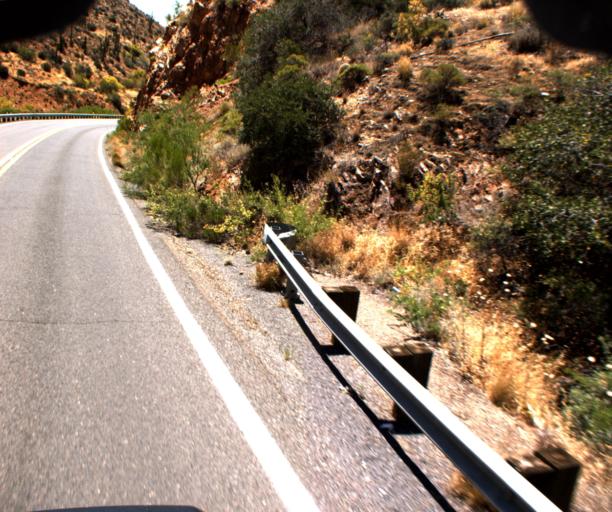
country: US
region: Arizona
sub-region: Pinal County
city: Superior
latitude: 33.1996
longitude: -111.0555
